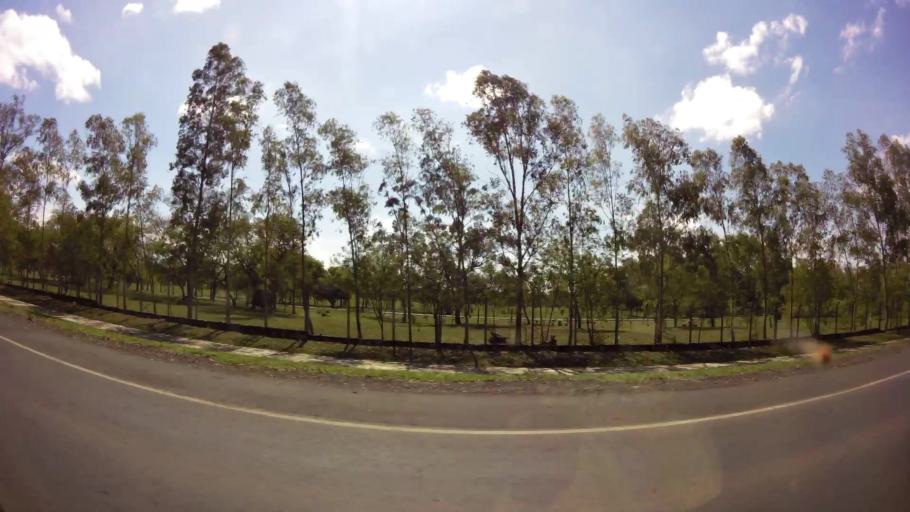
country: PY
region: Central
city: Fernando de la Mora
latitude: -25.2683
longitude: -57.5369
